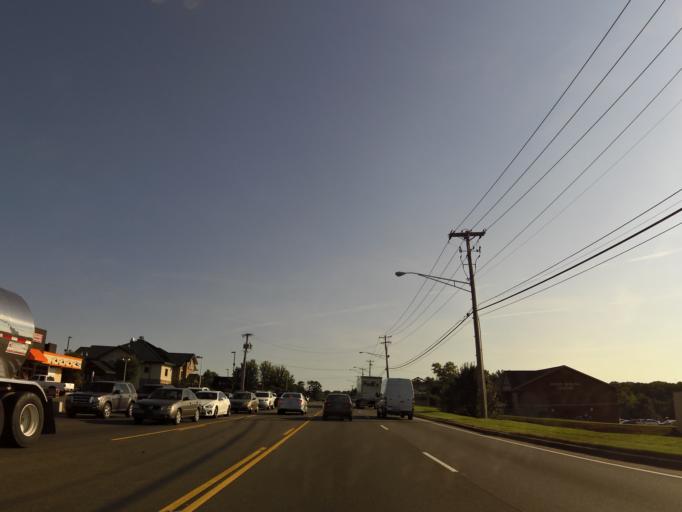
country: US
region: Tennessee
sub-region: Blount County
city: Maryville
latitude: 35.7308
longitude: -83.9966
